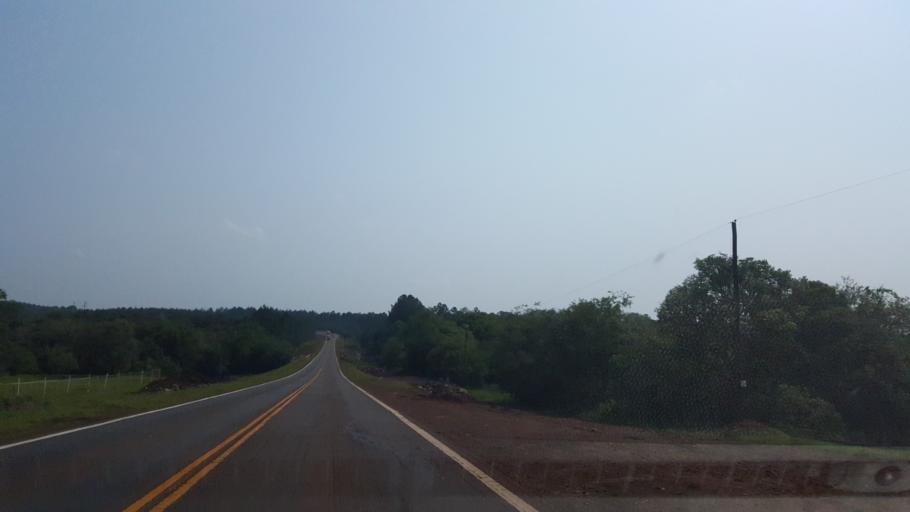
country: AR
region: Misiones
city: Santa Ana
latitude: -27.3860
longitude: -55.5914
